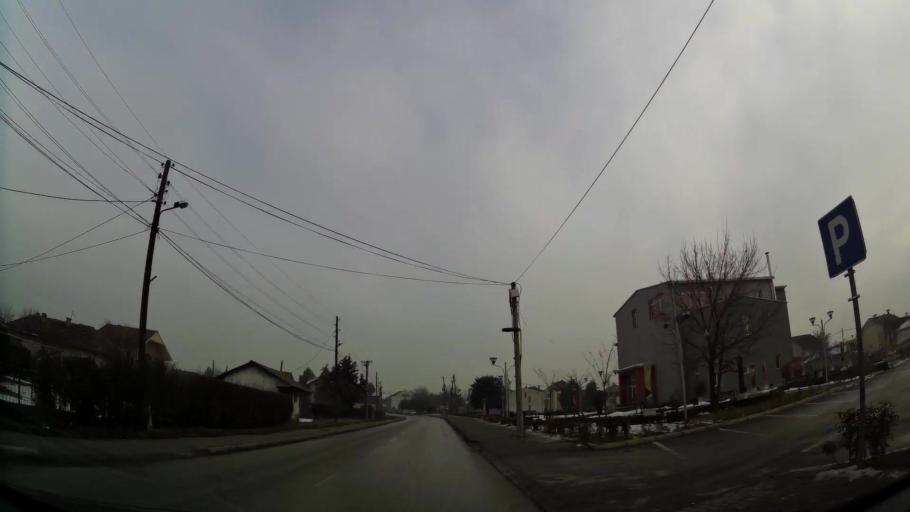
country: MK
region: Ilinden
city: Ilinden
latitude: 41.9948
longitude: 21.5729
